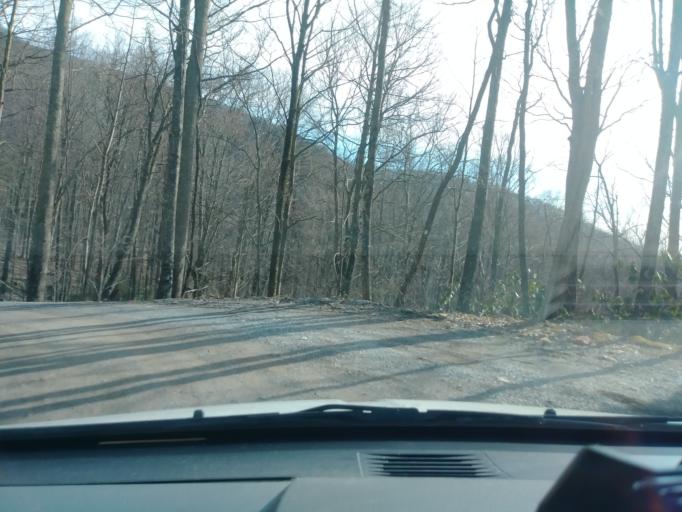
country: US
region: Tennessee
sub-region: Greene County
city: Tusculum
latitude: 36.0267
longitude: -82.7282
